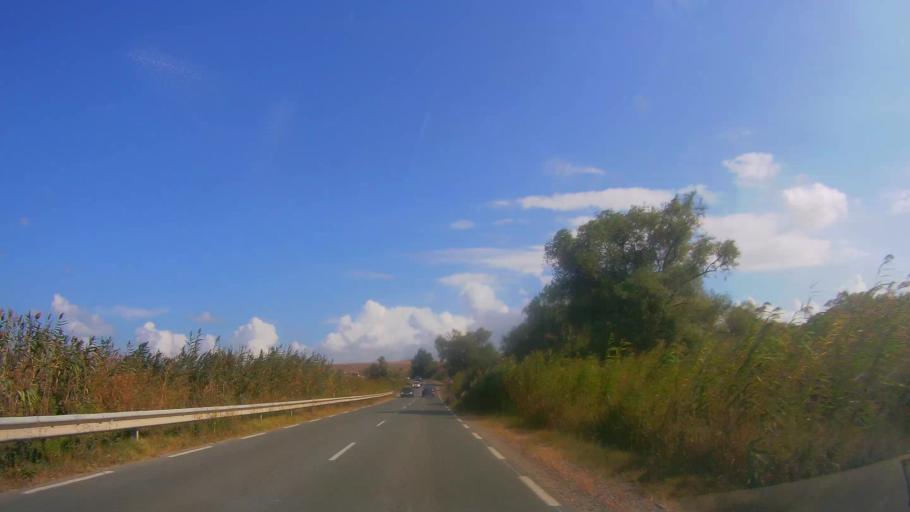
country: BG
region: Burgas
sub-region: Obshtina Burgas
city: Burgas
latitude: 42.4746
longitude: 27.3600
